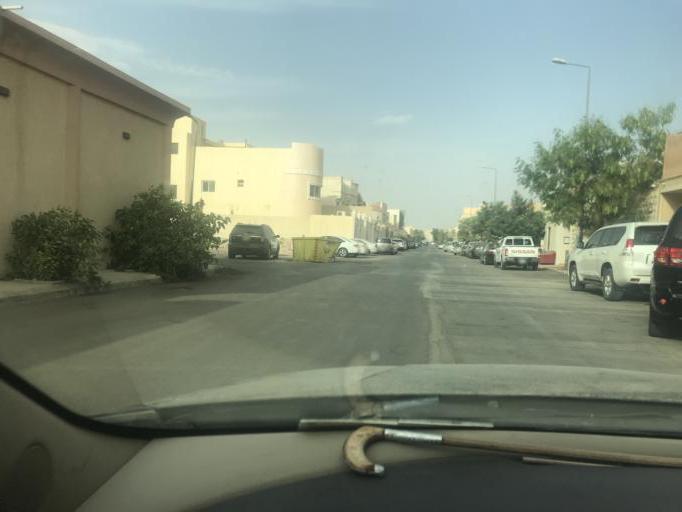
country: SA
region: Ar Riyad
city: Riyadh
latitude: 24.7974
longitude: 46.6694
